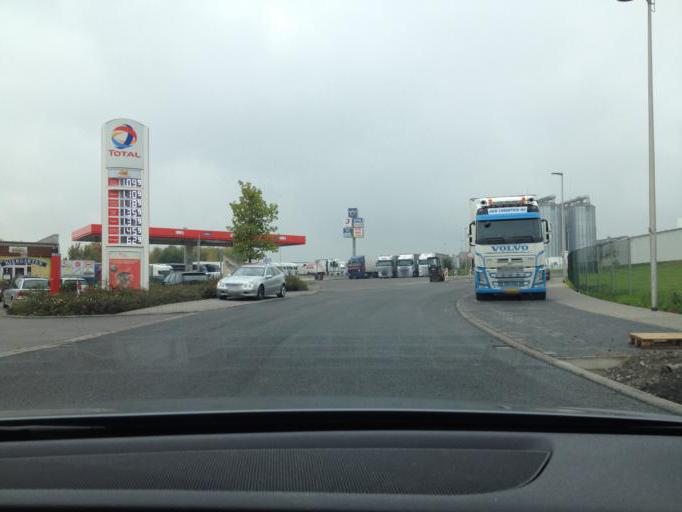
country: DE
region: Baden-Wuerttemberg
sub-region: Regierungsbezirk Stuttgart
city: Bad Rappenau
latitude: 49.2127
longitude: 9.0777
